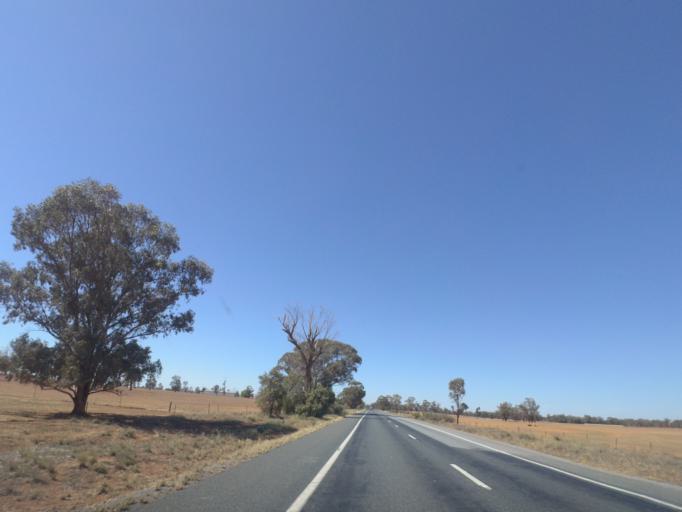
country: AU
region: New South Wales
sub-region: Bland
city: West Wyalong
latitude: -34.1880
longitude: 147.1122
